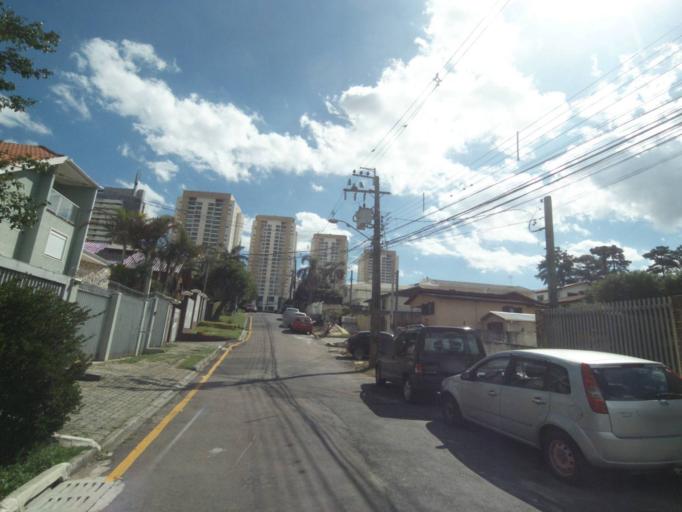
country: BR
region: Parana
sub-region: Curitiba
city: Curitiba
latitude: -25.4390
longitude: -49.3454
